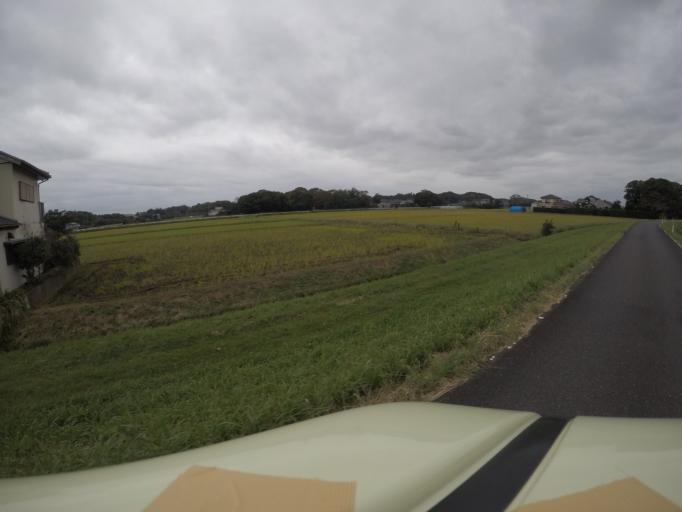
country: JP
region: Ibaraki
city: Inashiki
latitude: 35.9823
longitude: 140.3887
